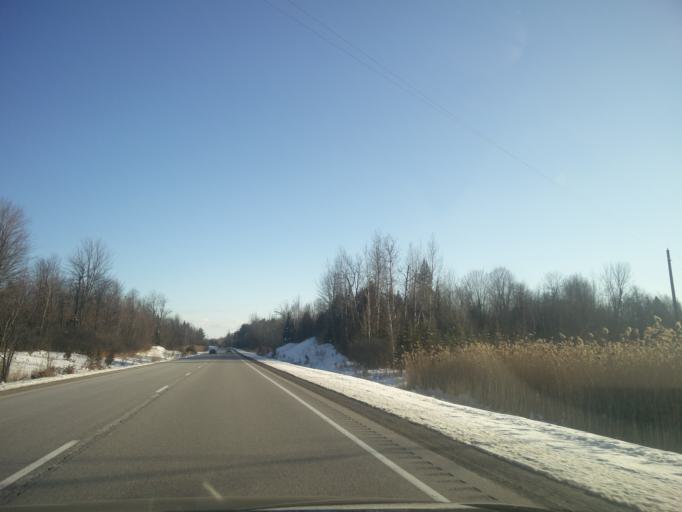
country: CA
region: Ontario
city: Prescott
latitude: 44.9177
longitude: -75.5759
